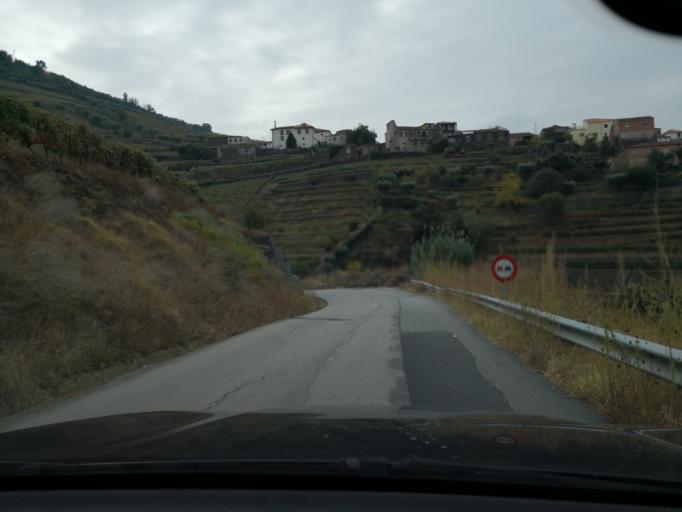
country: PT
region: Vila Real
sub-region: Peso da Regua
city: Peso da Regua
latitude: 41.1725
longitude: -7.7457
